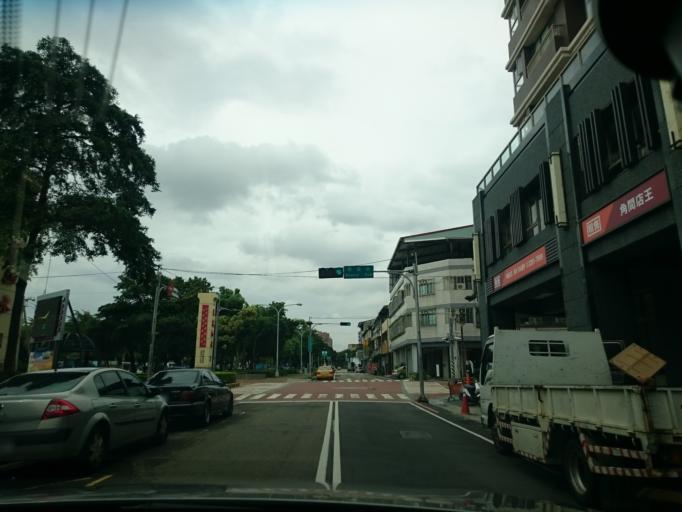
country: TW
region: Taiwan
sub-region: Taichung City
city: Taichung
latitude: 24.1399
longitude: 120.6972
